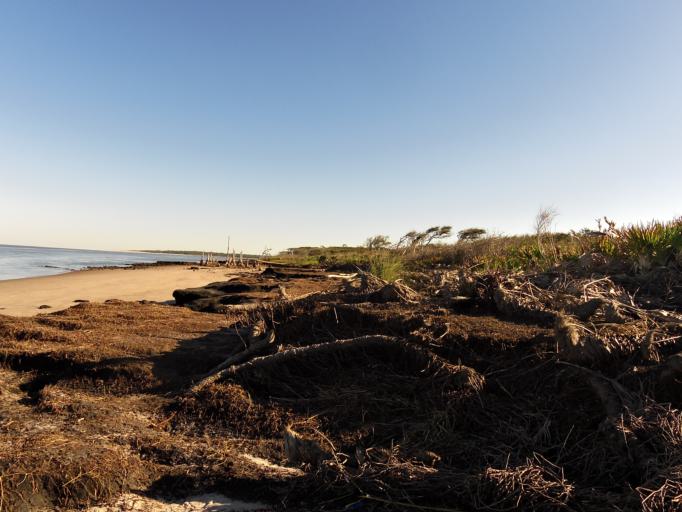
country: US
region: Florida
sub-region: Nassau County
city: Fernandina Beach
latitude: 30.5539
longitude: -81.4872
